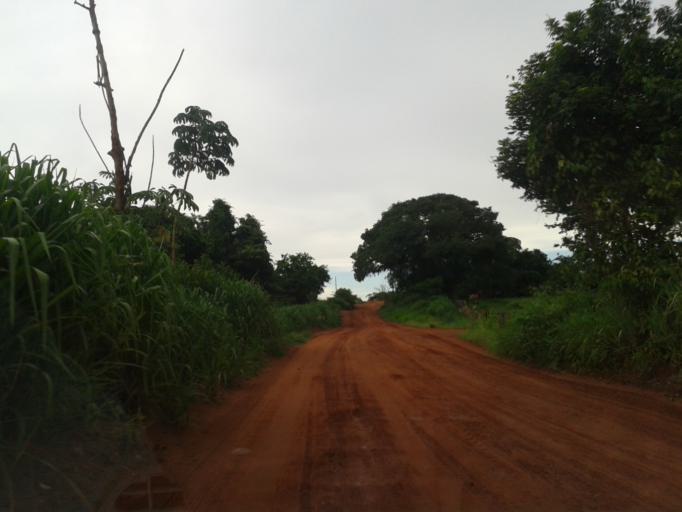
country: BR
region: Minas Gerais
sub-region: Santa Vitoria
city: Santa Vitoria
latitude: -19.1312
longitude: -50.5520
